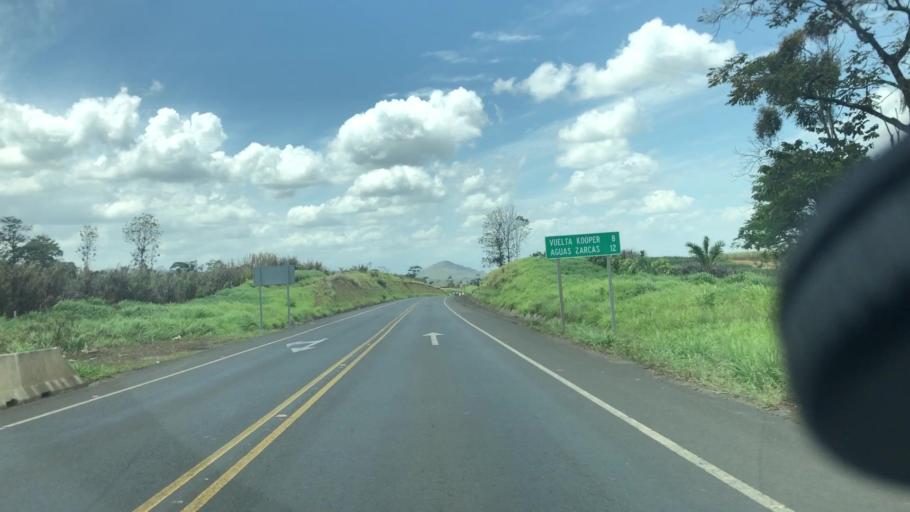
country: CR
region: Alajuela
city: Pital
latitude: 10.4344
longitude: -84.2803
